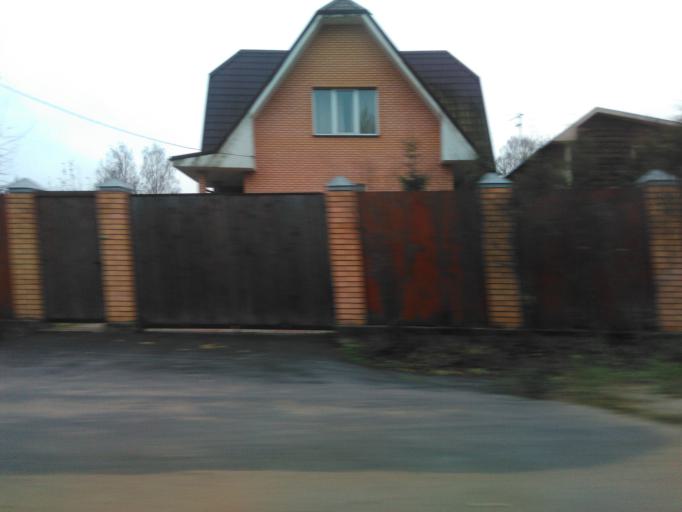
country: RU
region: Moskovskaya
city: Ashukino
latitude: 56.1592
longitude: 37.9538
